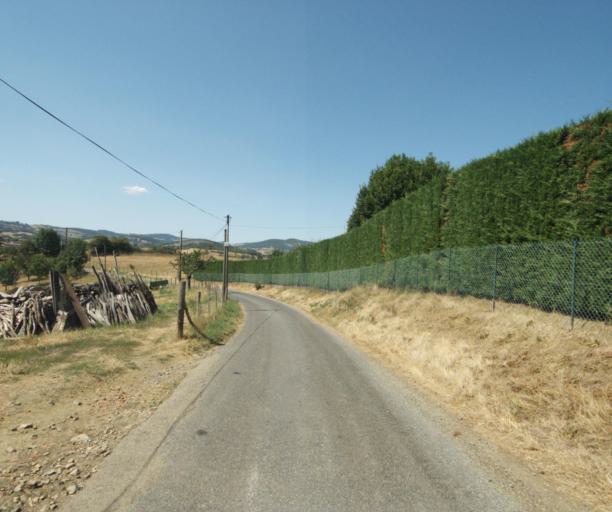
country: FR
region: Rhone-Alpes
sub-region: Departement du Rhone
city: Sainte-Foy-l'Argentiere
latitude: 45.7200
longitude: 4.5215
